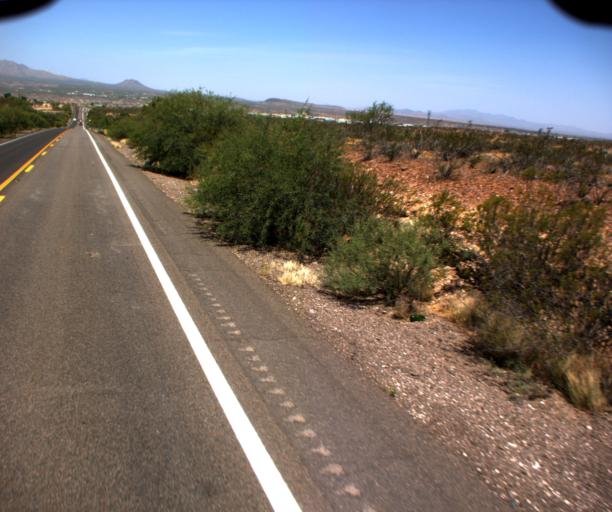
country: US
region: Arizona
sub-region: Gila County
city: Peridot
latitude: 33.2907
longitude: -110.4171
